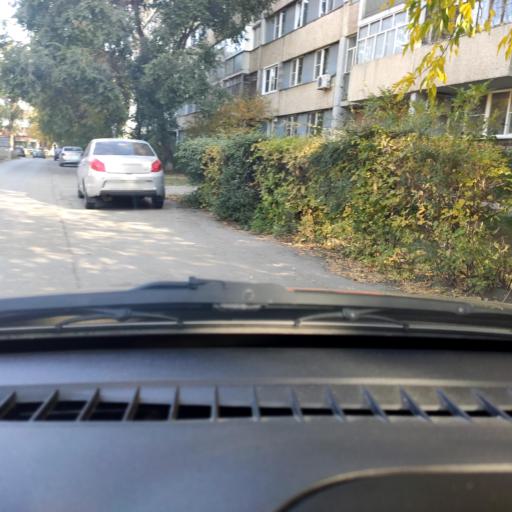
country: RU
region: Samara
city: Tol'yatti
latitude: 53.5379
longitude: 49.2677
